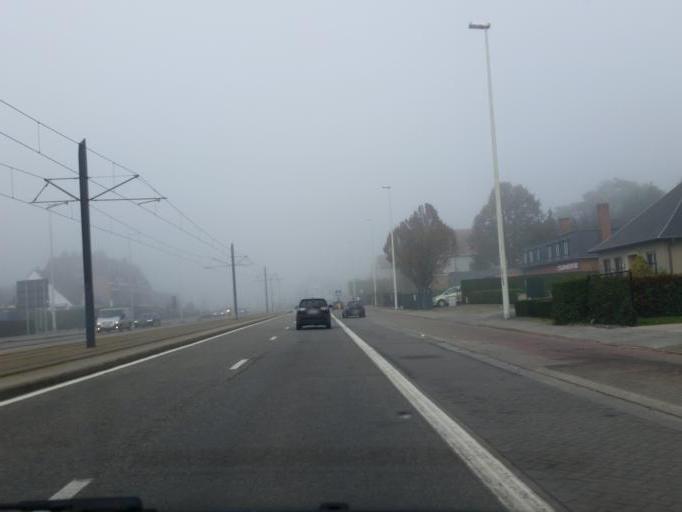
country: BE
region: Flanders
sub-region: Provincie Oost-Vlaanderen
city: Ledeberg
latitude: 51.0261
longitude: 3.7712
